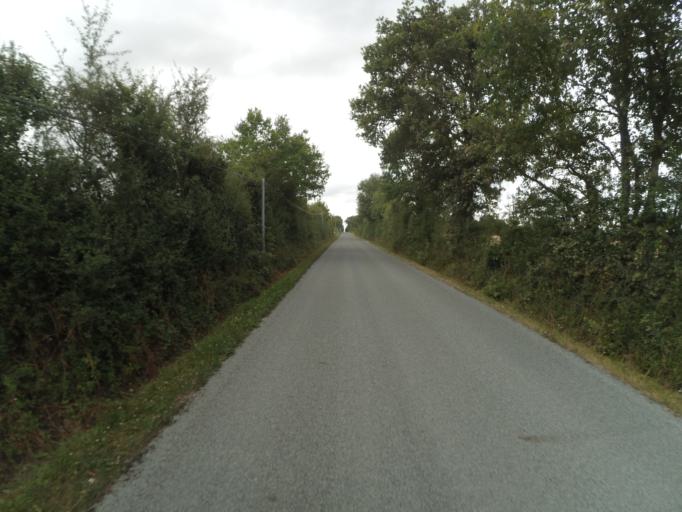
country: FR
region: Pays de la Loire
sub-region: Departement de la Vendee
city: Saint-Philbert-de-Bouaine
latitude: 46.9994
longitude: -1.5000
